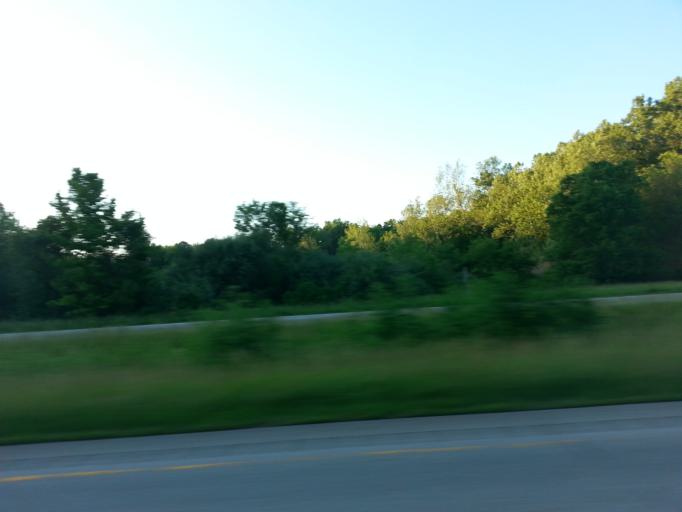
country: US
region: Indiana
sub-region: Fountain County
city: Covington
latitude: 40.1220
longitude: -87.4190
